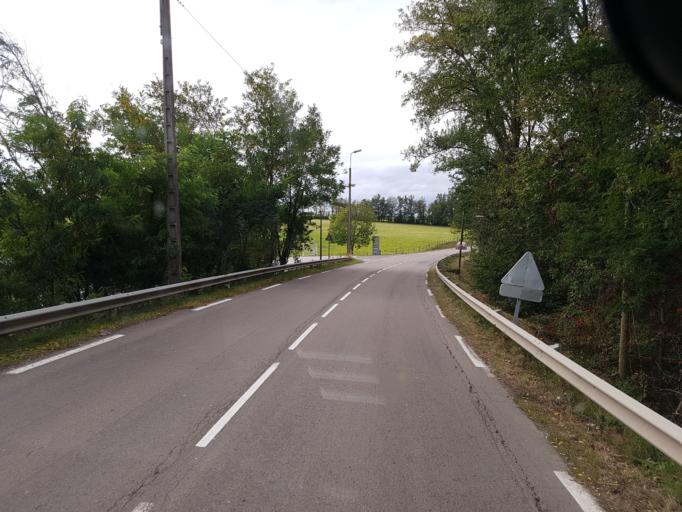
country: FR
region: Rhone-Alpes
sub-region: Departement de la Loire
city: La Ricamarie
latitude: 45.4153
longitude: 4.3073
